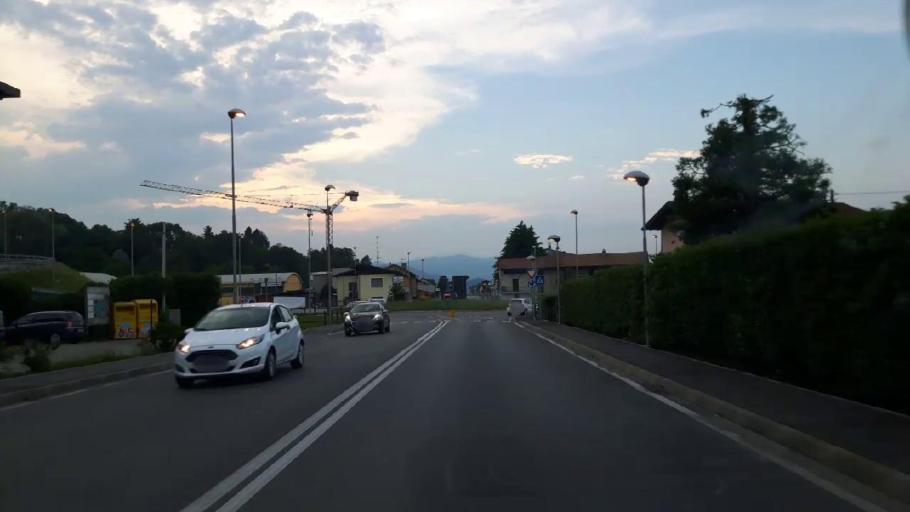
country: IT
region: Piedmont
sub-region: Provincia di Novara
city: Dormelletto
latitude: 45.7299
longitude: 8.5776
